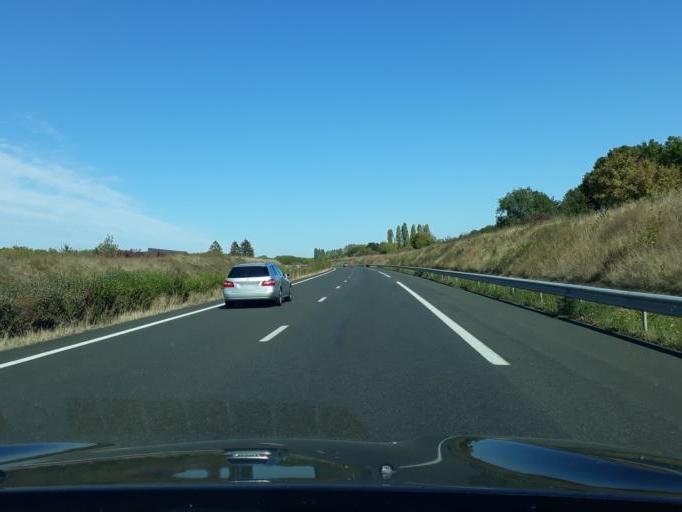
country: FR
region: Centre
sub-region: Departement d'Indre-et-Loire
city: Ballan-Mire
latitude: 47.3223
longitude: 0.6010
